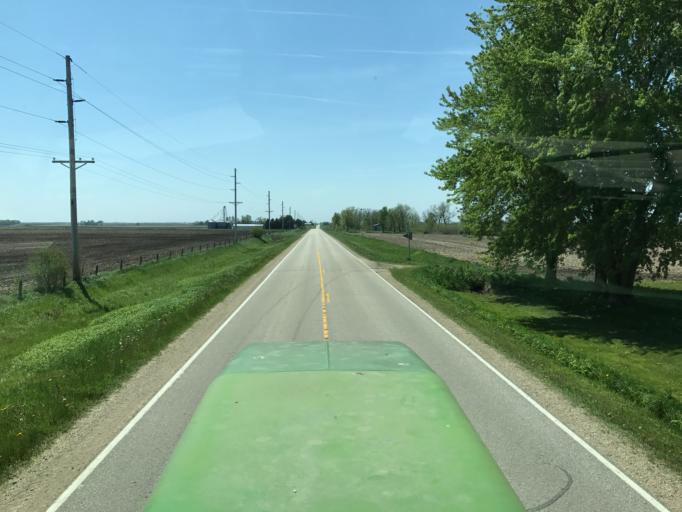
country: US
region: Iowa
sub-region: Butler County
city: Shell Rock
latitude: 42.6780
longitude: -92.5936
